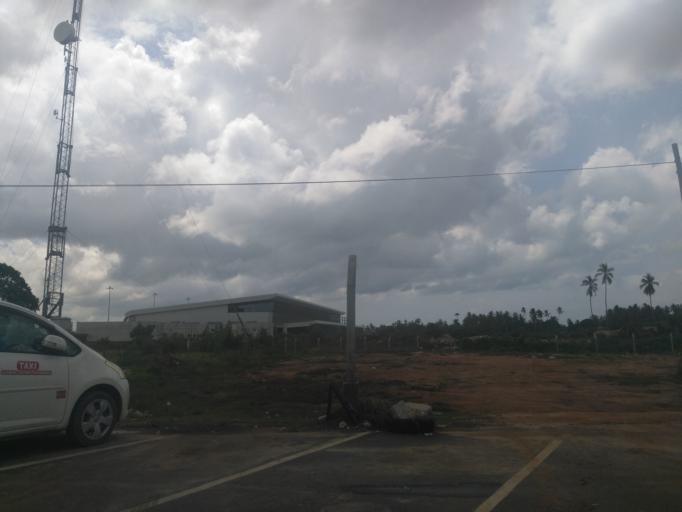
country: TZ
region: Zanzibar Urban/West
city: Zanzibar
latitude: -6.2191
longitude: 39.2205
